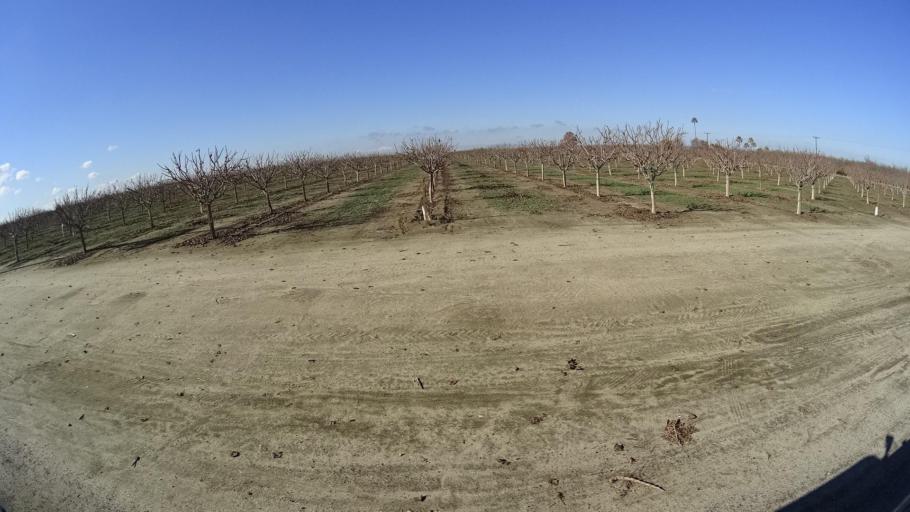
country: US
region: California
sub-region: Kern County
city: Delano
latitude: 35.7313
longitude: -119.2584
